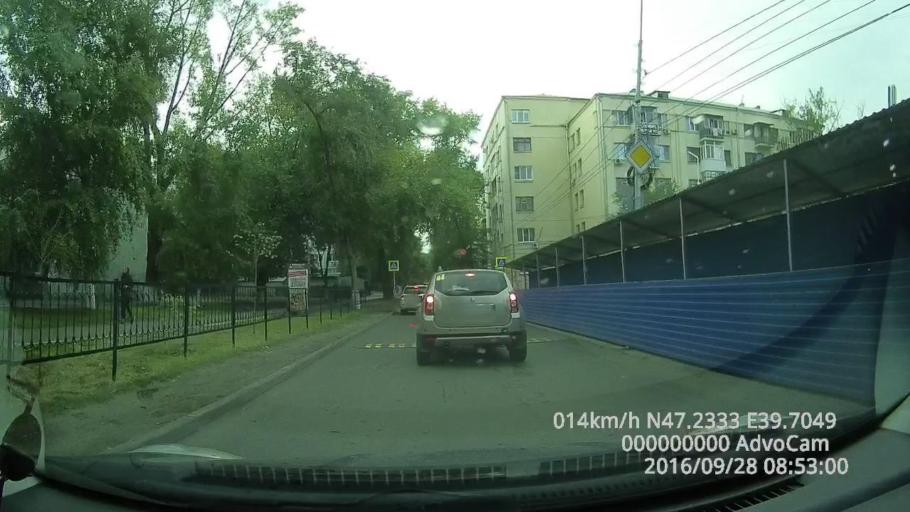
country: RU
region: Rostov
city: Rostov-na-Donu
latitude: 47.2333
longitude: 39.7050
